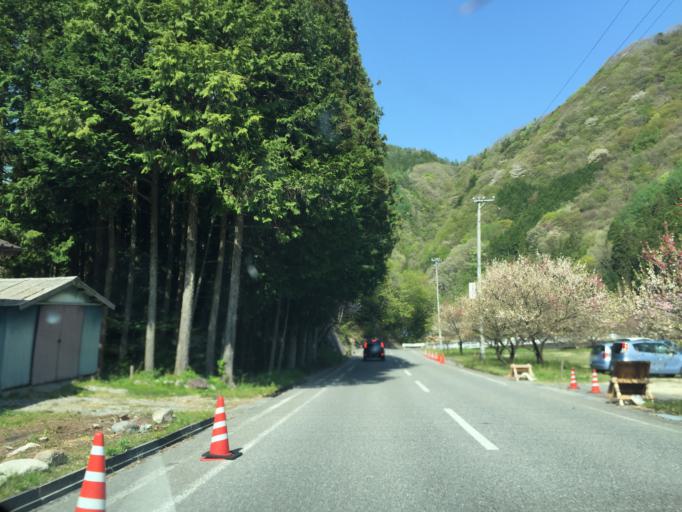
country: JP
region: Gifu
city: Nakatsugawa
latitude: 35.4470
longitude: 137.6664
